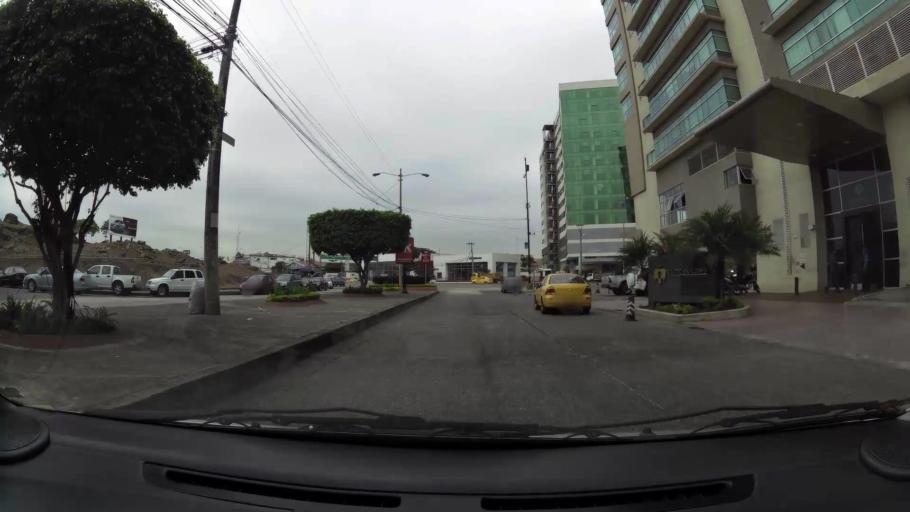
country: EC
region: Guayas
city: Eloy Alfaro
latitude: -2.1553
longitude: -79.8896
